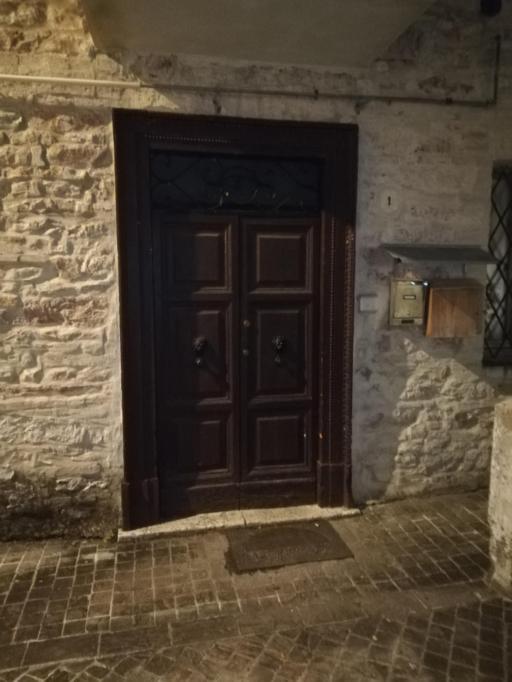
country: IT
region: The Marches
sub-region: Provincia di Ancona
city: Genga
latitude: 43.4288
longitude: 12.9354
